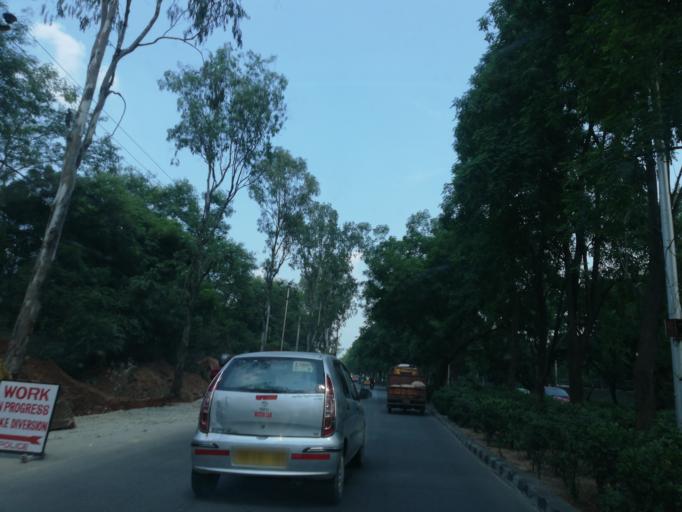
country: IN
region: Telangana
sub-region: Medak
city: Serilingampalle
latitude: 17.4540
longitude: 78.3425
